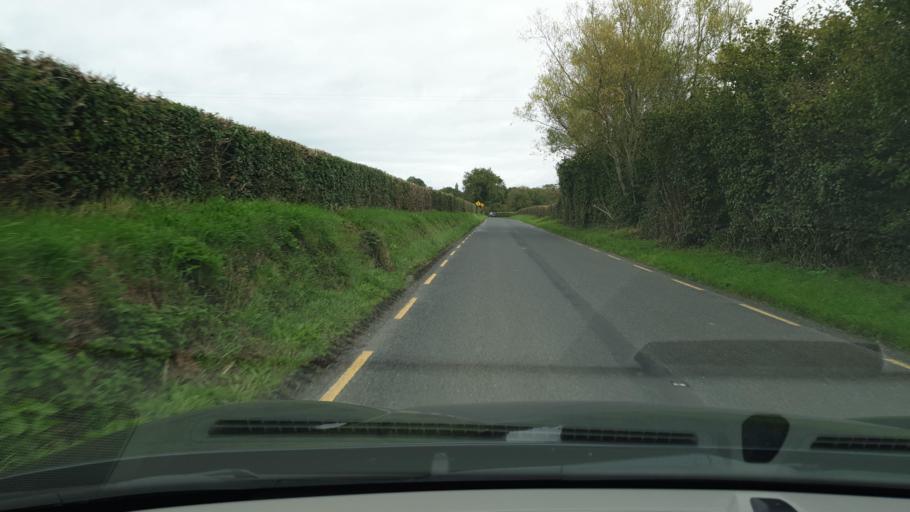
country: IE
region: Leinster
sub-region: Kildare
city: Maynooth
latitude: 53.3787
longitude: -6.6241
